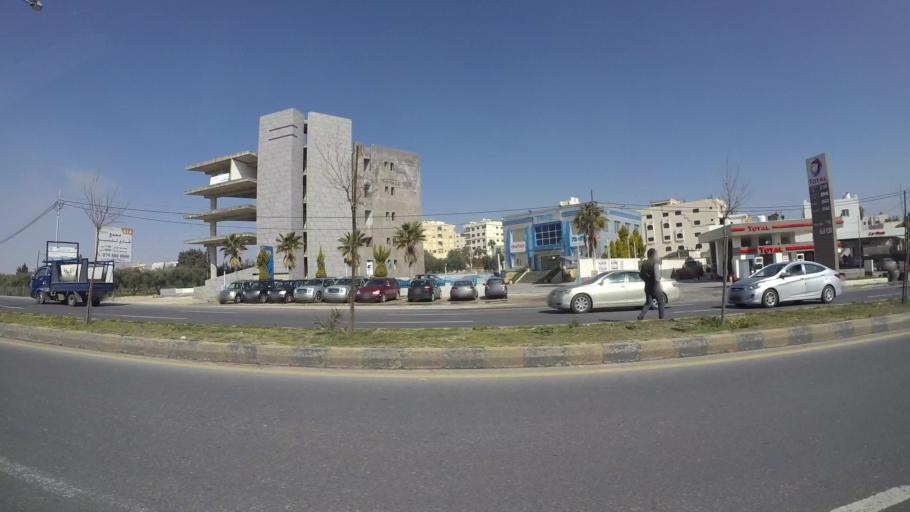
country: JO
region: Amman
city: Al Bunayyat ash Shamaliyah
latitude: 31.9014
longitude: 35.8731
